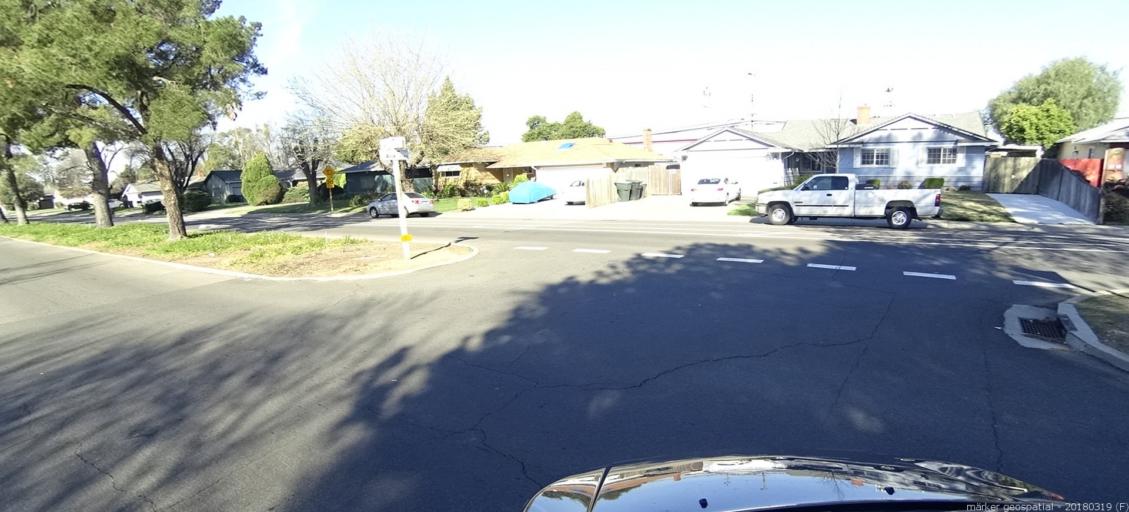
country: US
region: California
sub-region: Sacramento County
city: Parkway
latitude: 38.4921
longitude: -121.4544
